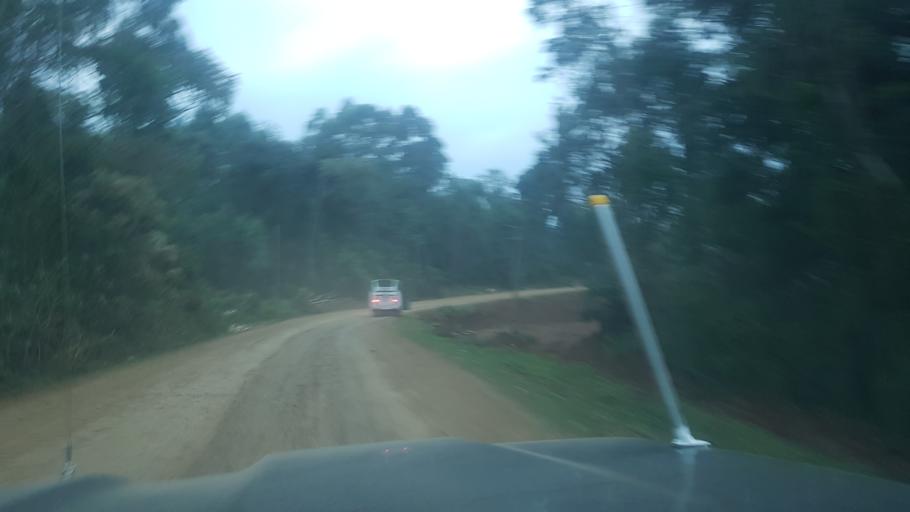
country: ET
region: Oromiya
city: Gore
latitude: 7.7868
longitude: 35.4586
